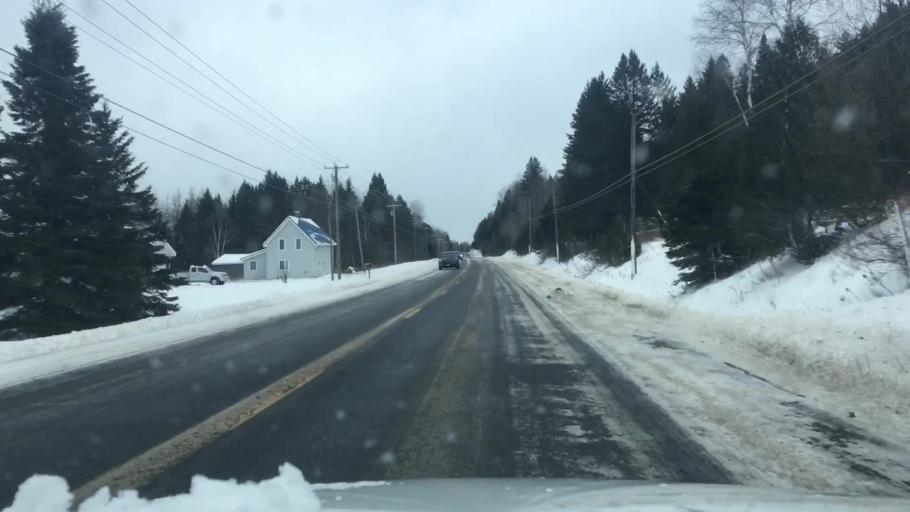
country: US
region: Maine
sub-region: Aroostook County
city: Madawaska
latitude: 47.3308
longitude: -68.1993
